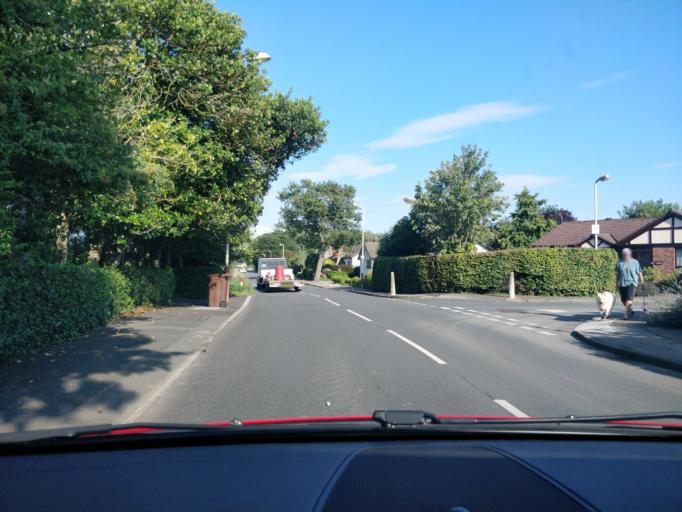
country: GB
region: England
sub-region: Sefton
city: Southport
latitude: 53.6533
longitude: -2.9578
